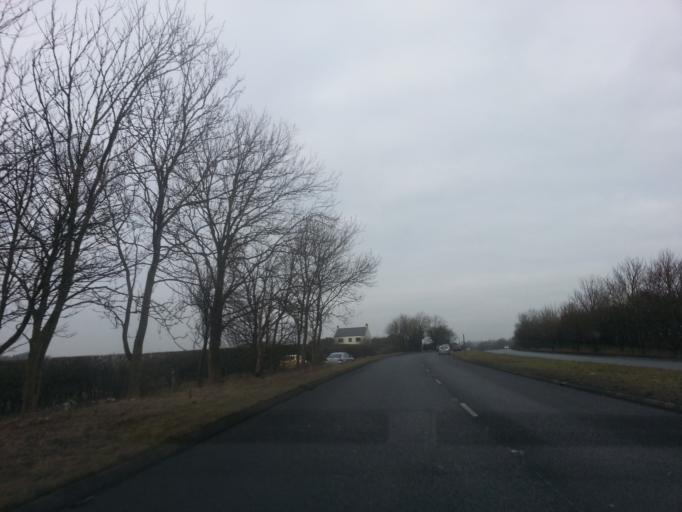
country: GB
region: England
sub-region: Darlington
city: Heighington
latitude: 54.5706
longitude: -1.6093
